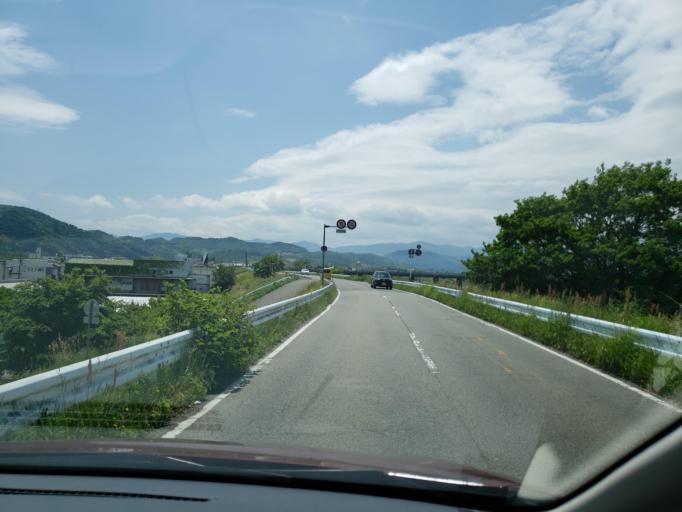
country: JP
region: Tokushima
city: Tokushima-shi
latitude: 34.0791
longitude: 134.5024
